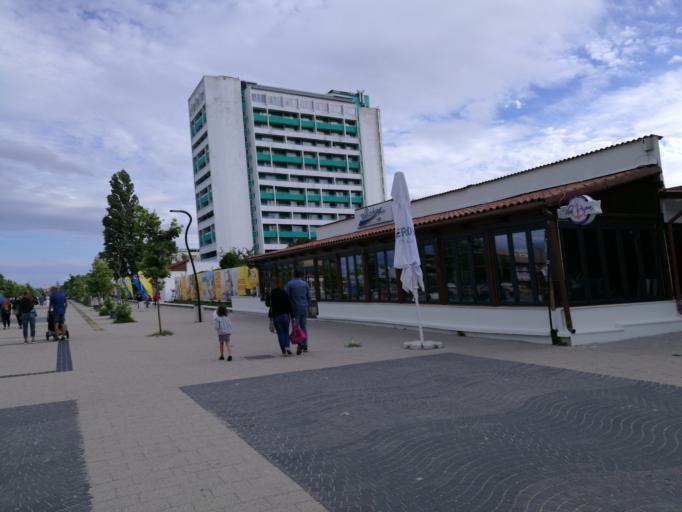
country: RO
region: Constanta
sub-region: Municipiul Constanta
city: Palazu Mare
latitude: 44.2461
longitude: 28.6222
